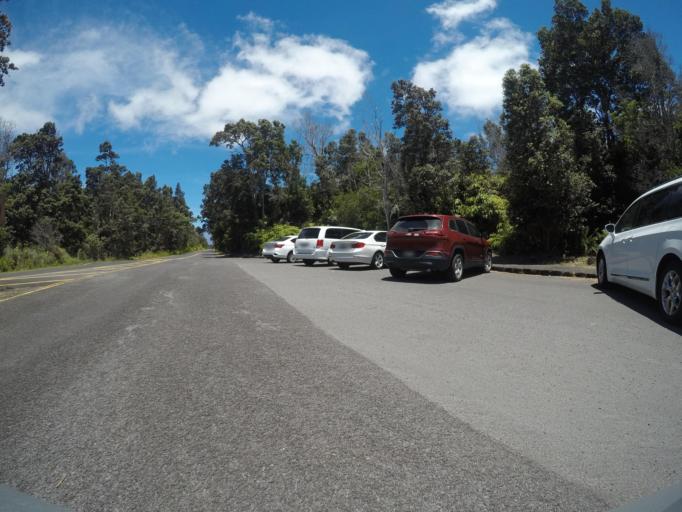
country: US
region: Hawaii
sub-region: Hawaii County
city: Volcano
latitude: 19.3653
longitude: -155.2166
